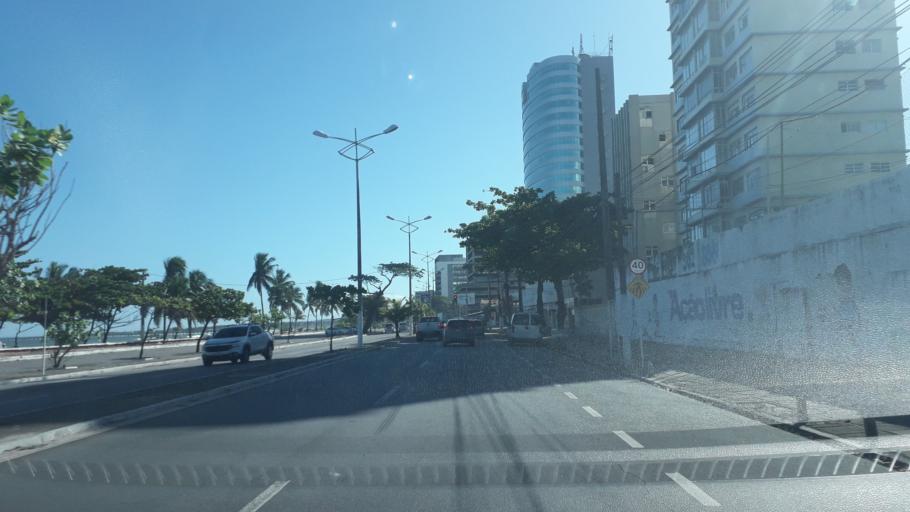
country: BR
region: Alagoas
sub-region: Maceio
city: Maceio
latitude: -9.6696
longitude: -35.7344
